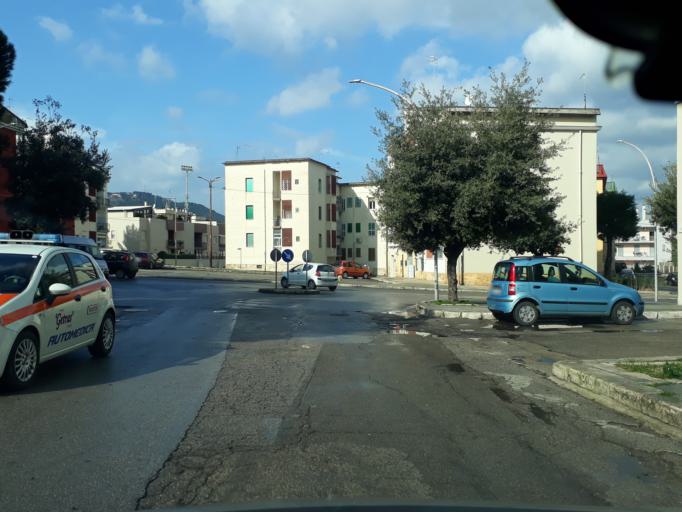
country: IT
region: Apulia
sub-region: Provincia di Brindisi
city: Fasano
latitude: 40.8283
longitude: 17.3561
